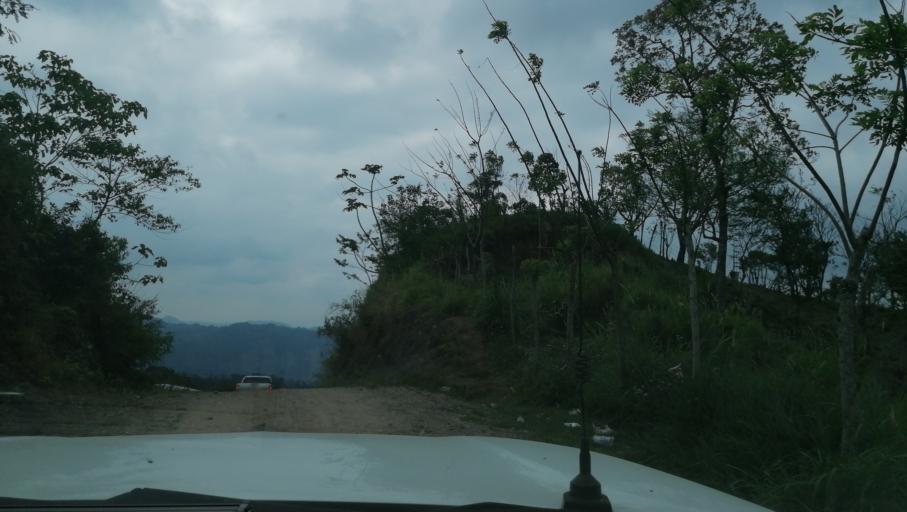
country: MX
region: Chiapas
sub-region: Francisco Leon
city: San Miguel la Sardina
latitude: 17.3452
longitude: -93.3114
